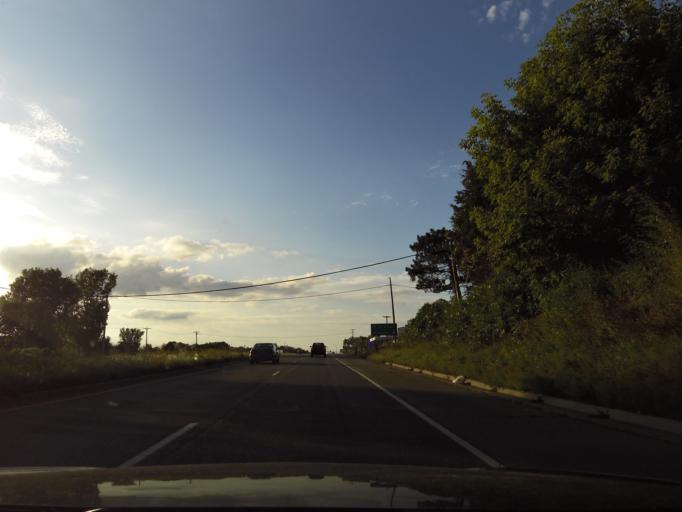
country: US
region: Minnesota
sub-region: Dakota County
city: Hastings
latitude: 44.7638
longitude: -92.8556
